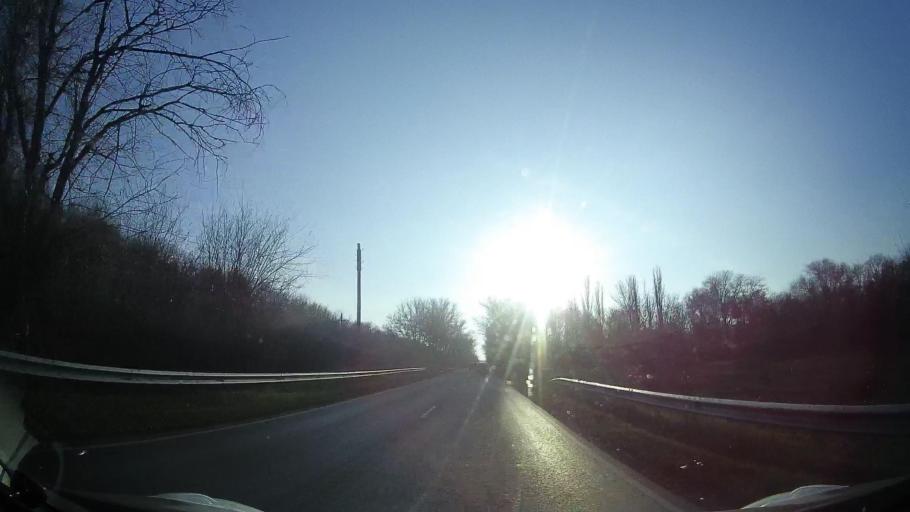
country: RU
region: Rostov
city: Ol'ginskaya
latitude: 47.1726
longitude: 39.9472
